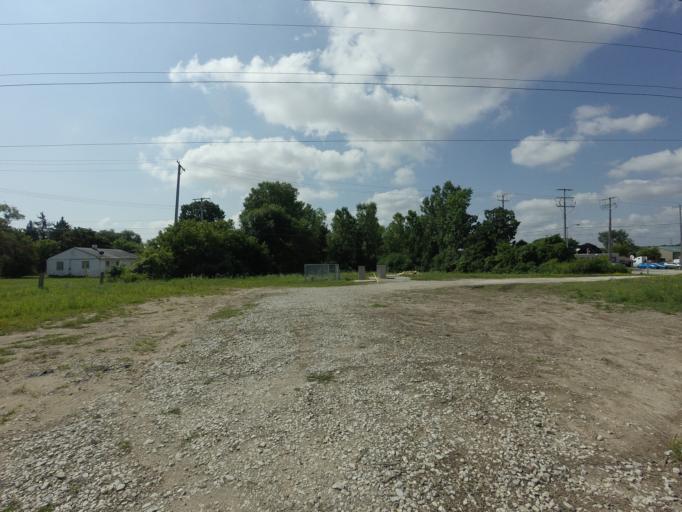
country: US
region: Wisconsin
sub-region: Milwaukee County
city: Saint Francis
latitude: 42.9705
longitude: -87.9188
